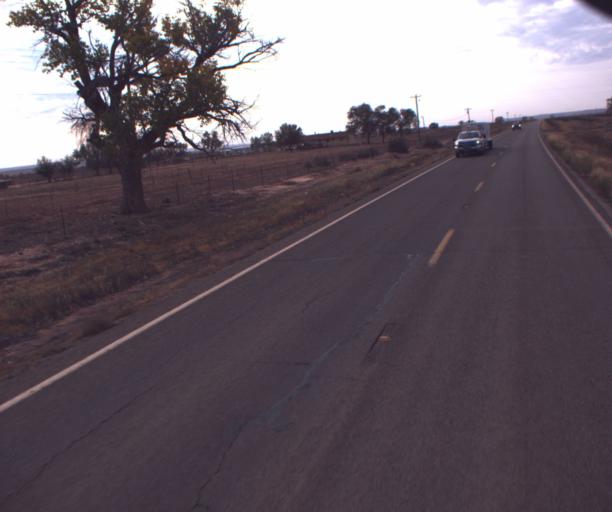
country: US
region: Arizona
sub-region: Apache County
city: Many Farms
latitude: 36.4199
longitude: -109.6064
